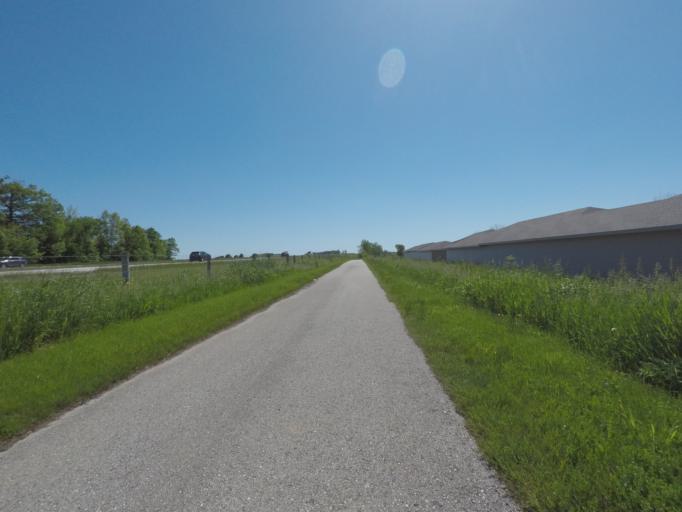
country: US
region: Wisconsin
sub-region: Sheboygan County
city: Sheboygan Falls
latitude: 43.7504
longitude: -87.8294
